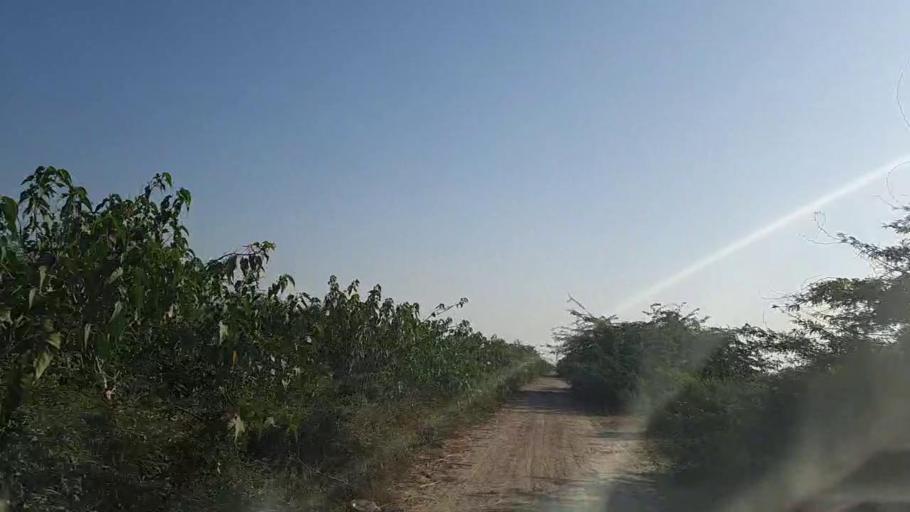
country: PK
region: Sindh
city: Jati
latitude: 24.3993
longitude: 68.2301
